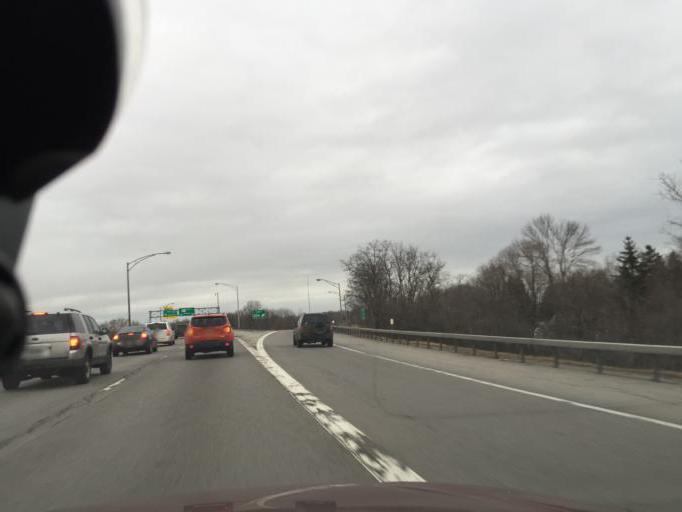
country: US
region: New York
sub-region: Monroe County
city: North Gates
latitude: 43.1539
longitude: -77.6791
